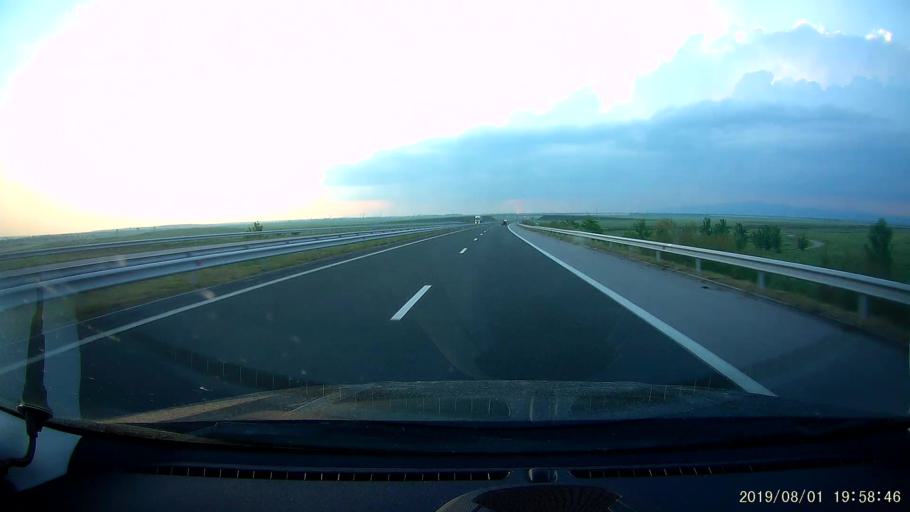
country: BG
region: Yambol
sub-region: Obshtina Straldzha
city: Straldzha
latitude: 42.5462
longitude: 26.7536
